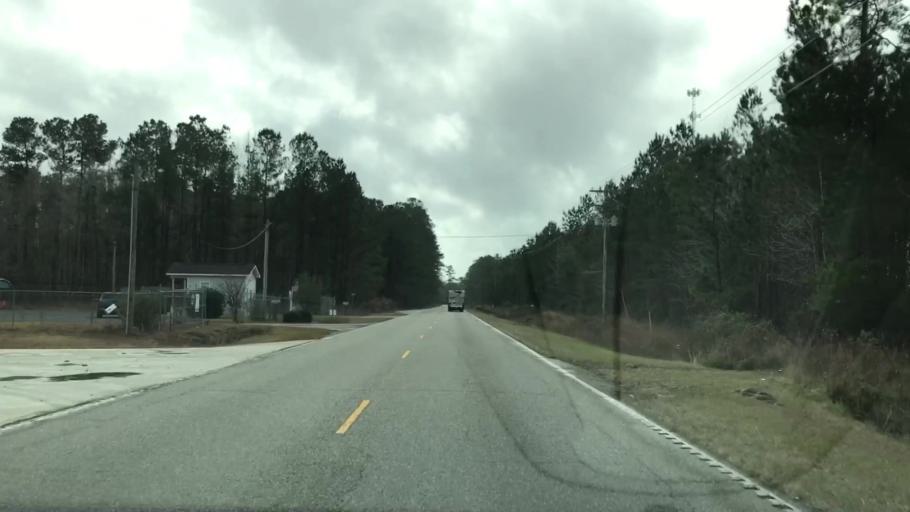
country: US
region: South Carolina
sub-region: Georgetown County
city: Murrells Inlet
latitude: 33.6253
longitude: -79.1910
